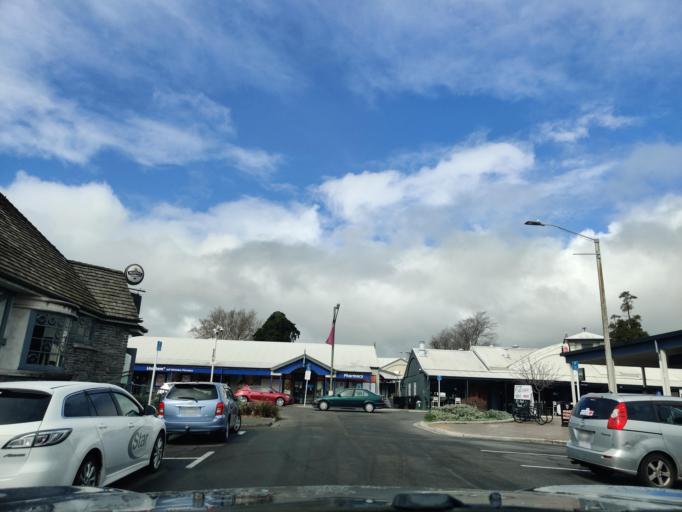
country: NZ
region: Hawke's Bay
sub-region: Hastings District
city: Hastings
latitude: -39.6691
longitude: 176.8777
